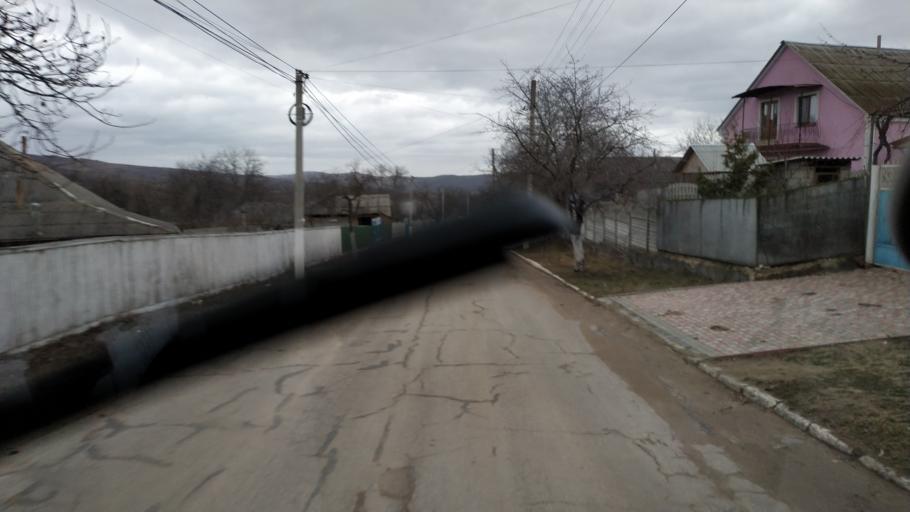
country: MD
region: Calarasi
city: Calarasi
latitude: 47.2616
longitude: 28.1349
